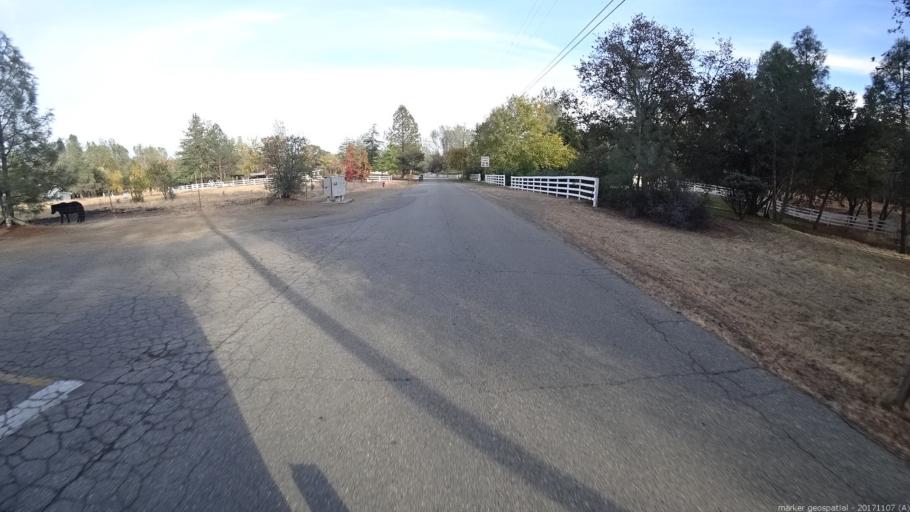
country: US
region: California
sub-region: Shasta County
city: Shasta
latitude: 40.5264
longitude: -122.4826
